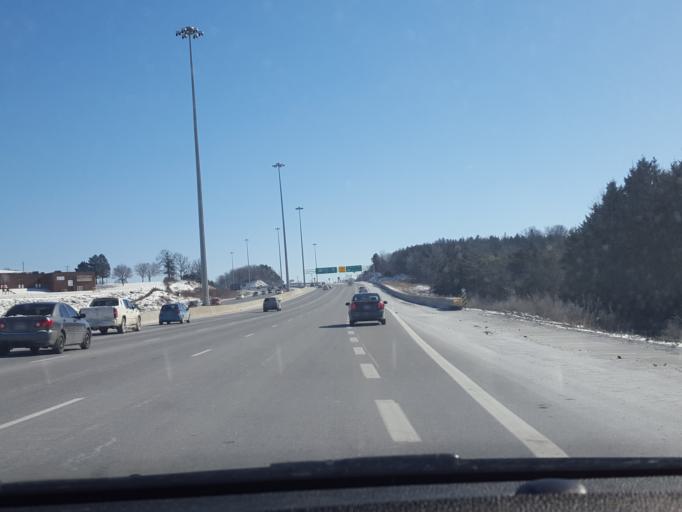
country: CA
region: Ontario
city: Kitchener
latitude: 43.4183
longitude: -80.4127
